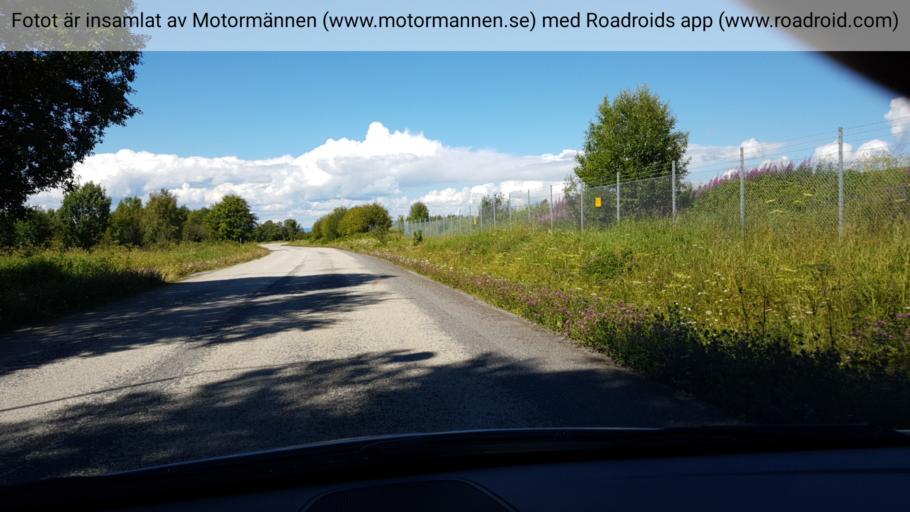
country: SE
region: Jaemtland
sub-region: Krokoms Kommun
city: Krokom
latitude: 63.1983
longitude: 14.4744
